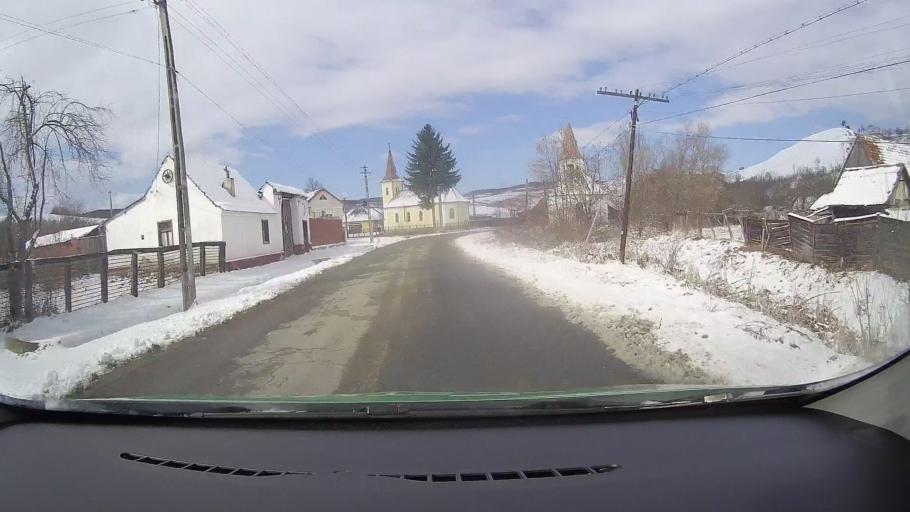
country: RO
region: Sibiu
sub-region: Comuna Altina
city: Altina
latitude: 45.9832
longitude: 24.4561
